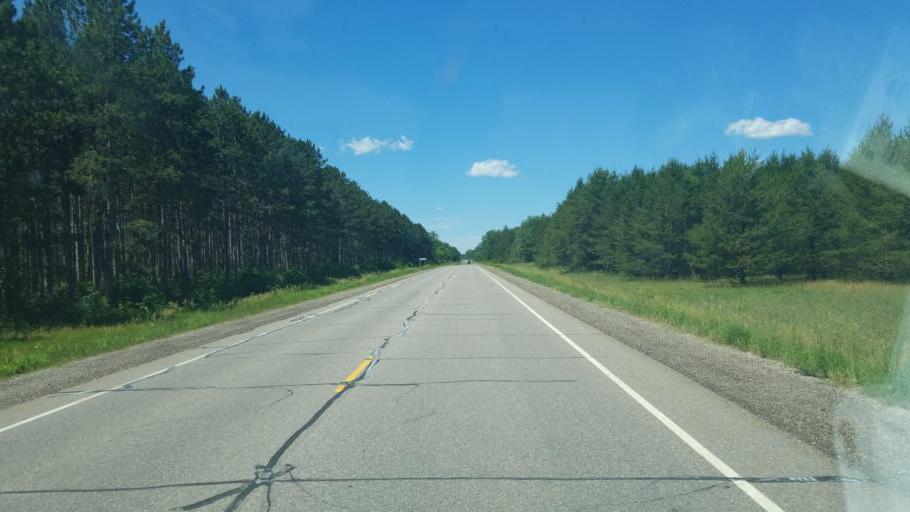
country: US
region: Wisconsin
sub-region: Adams County
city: Friendship
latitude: 44.0470
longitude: -89.9964
